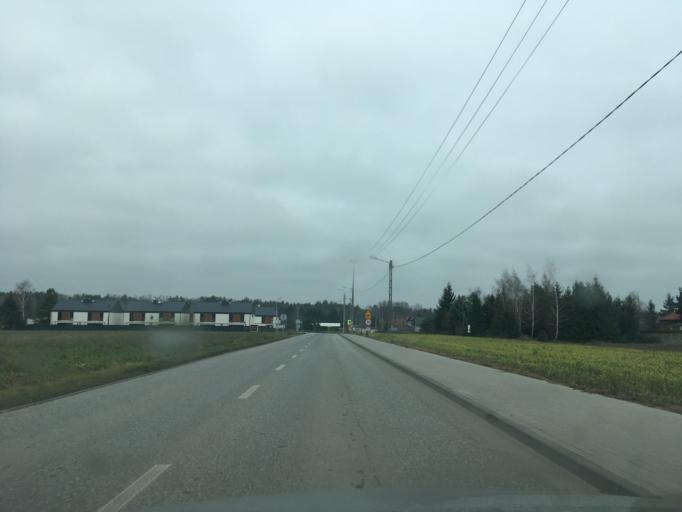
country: PL
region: Masovian Voivodeship
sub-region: Powiat piaseczynski
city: Lesznowola
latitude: 52.0723
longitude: 20.9353
